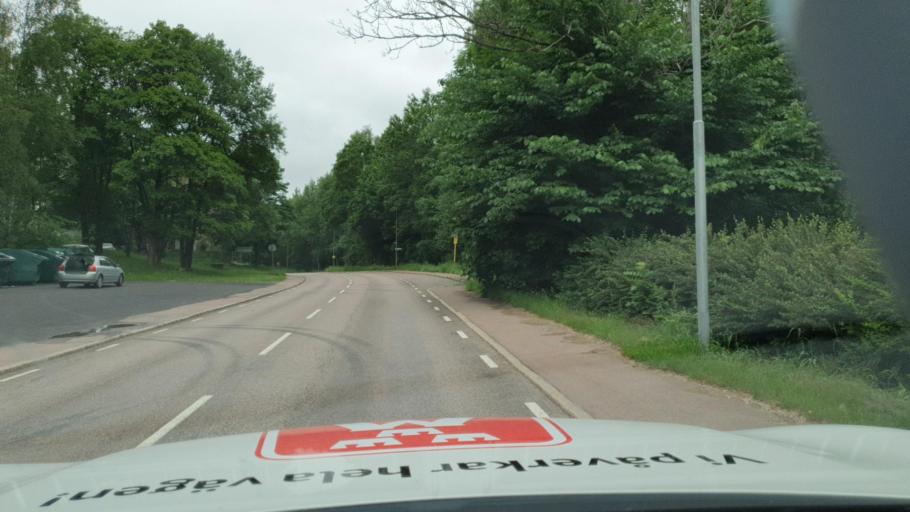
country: SE
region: Vaermland
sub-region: Karlstads Kommun
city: Edsvalla
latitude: 59.4397
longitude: 13.2099
